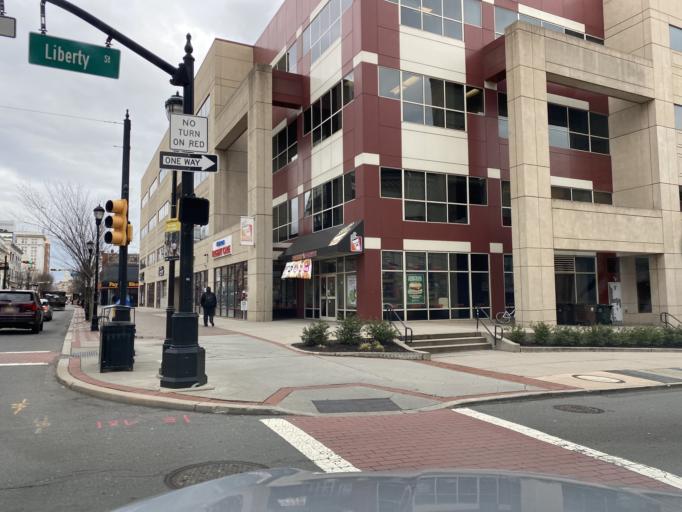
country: US
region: New Jersey
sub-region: Middlesex County
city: New Brunswick
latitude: 40.4936
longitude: -74.4436
